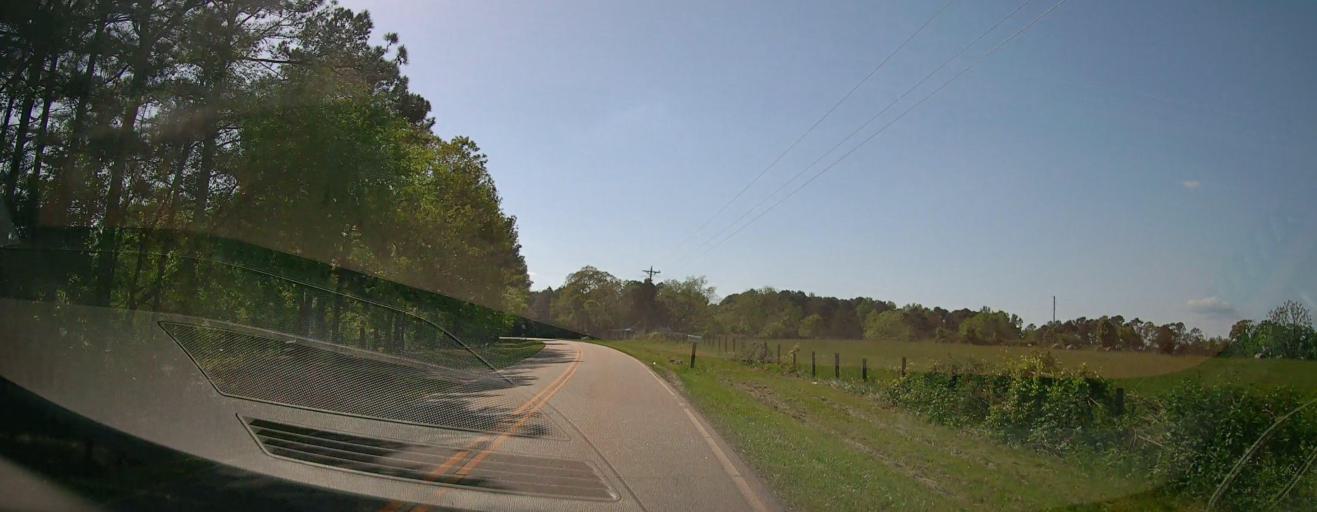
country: US
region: Georgia
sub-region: Morgan County
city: Madison
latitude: 33.6628
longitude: -83.4812
